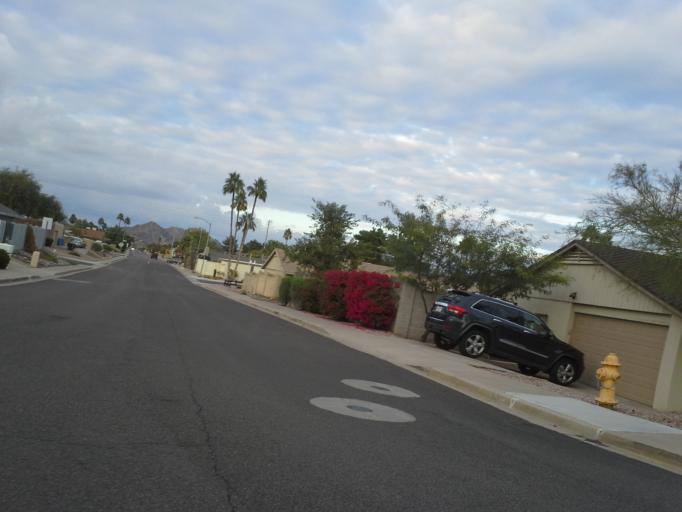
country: US
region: Arizona
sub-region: Maricopa County
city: Paradise Valley
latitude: 33.5806
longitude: -112.0306
